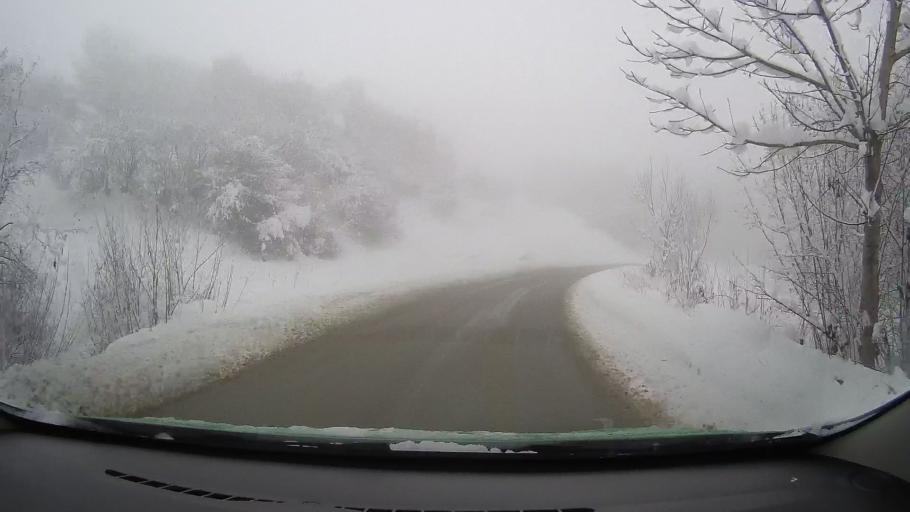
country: RO
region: Sibiu
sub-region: Comuna Poiana Sibiului
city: Poiana Sibiului
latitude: 45.7980
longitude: 23.7890
